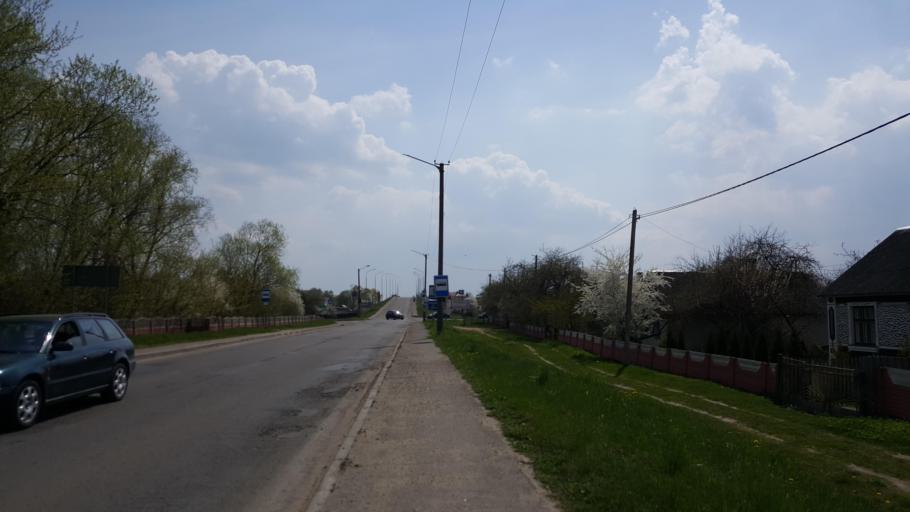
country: BY
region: Brest
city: Zhabinka
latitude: 52.2009
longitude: 24.0068
